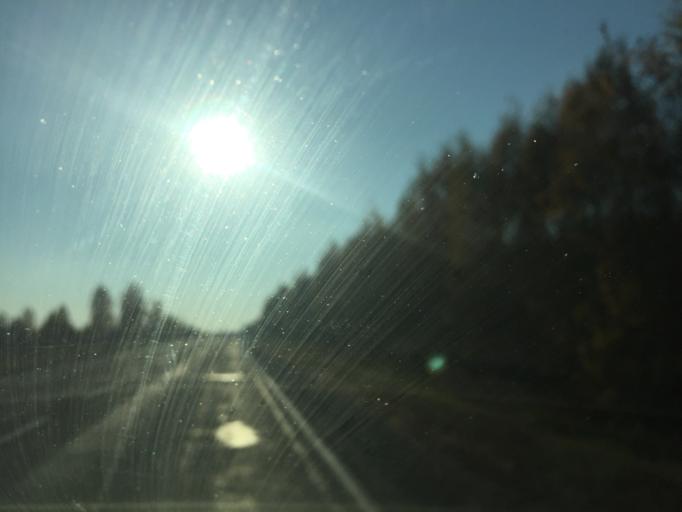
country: BY
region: Gomel
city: Dobrush
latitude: 52.3644
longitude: 31.2462
